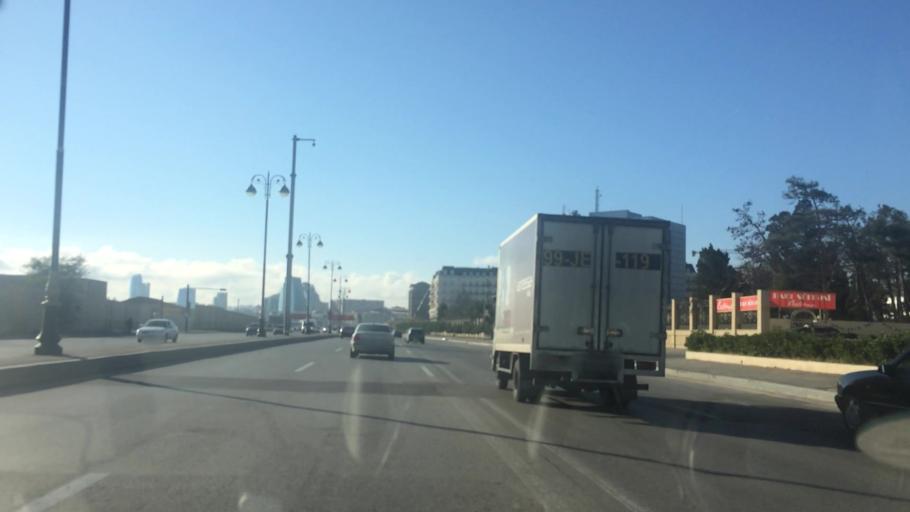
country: AZ
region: Baki
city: Baku
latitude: 40.3747
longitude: 49.8962
